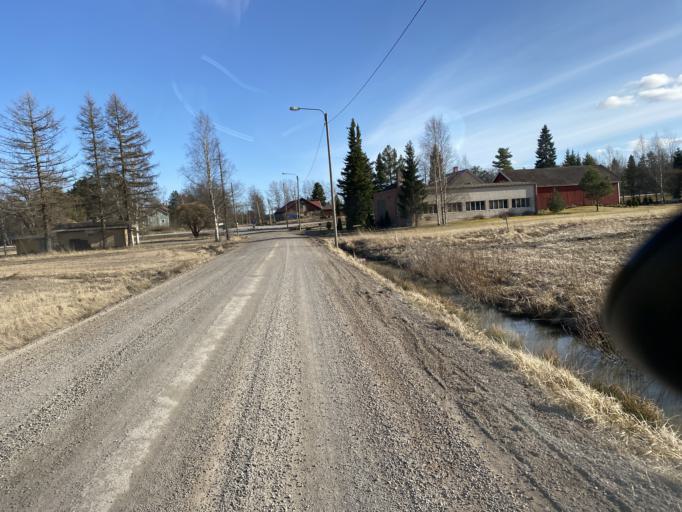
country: FI
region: Satakunta
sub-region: Rauma
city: Lappi
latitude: 61.1253
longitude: 21.9540
